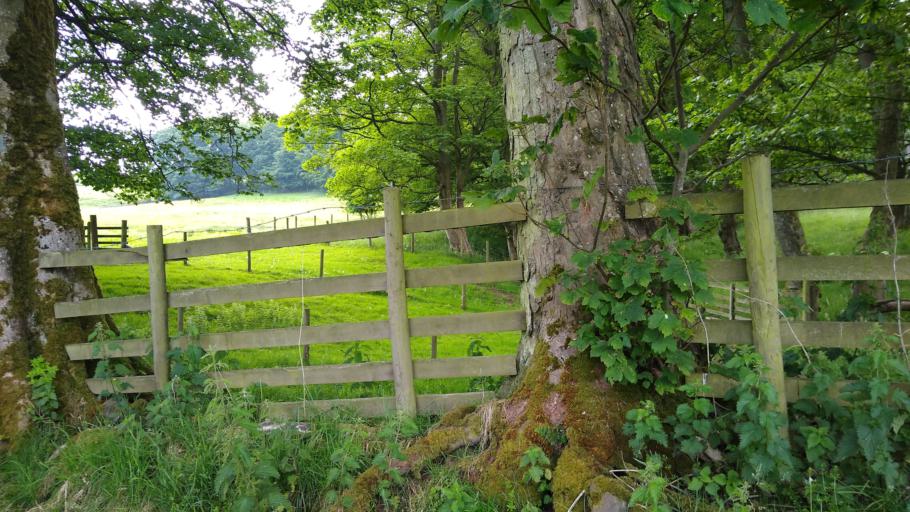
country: GB
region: England
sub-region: Northumberland
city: Greenhead
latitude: 54.9201
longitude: -2.6131
